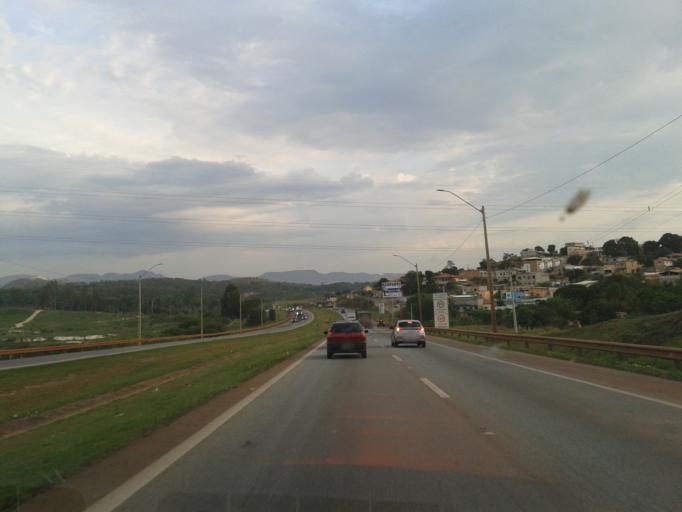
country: BR
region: Minas Gerais
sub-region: Betim
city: Betim
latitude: -19.9709
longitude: -44.1603
